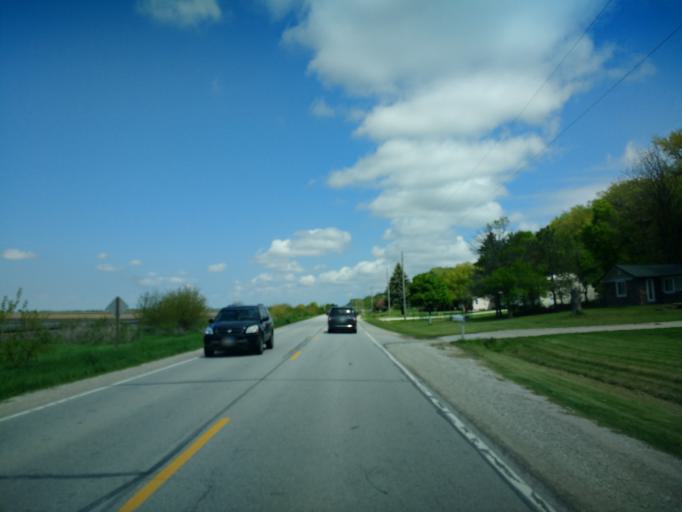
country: US
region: Iowa
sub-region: Harrison County
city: Missouri Valley
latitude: 41.4488
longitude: -95.8722
